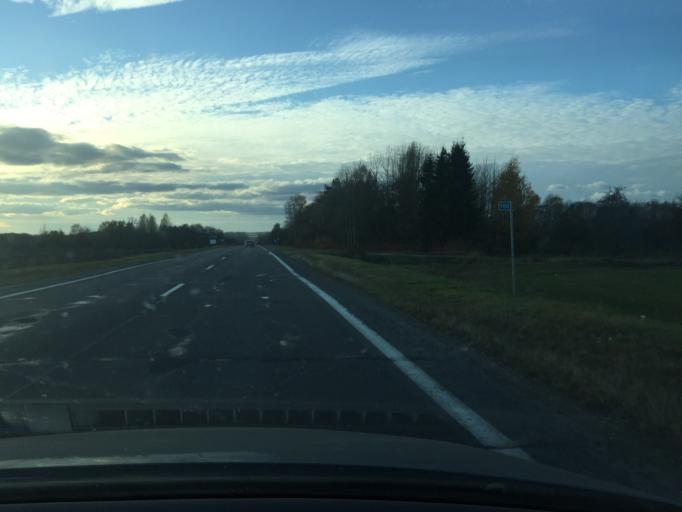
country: BY
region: Vitebsk
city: Vyerkhnyadzvinsk
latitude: 55.8373
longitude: 27.8946
